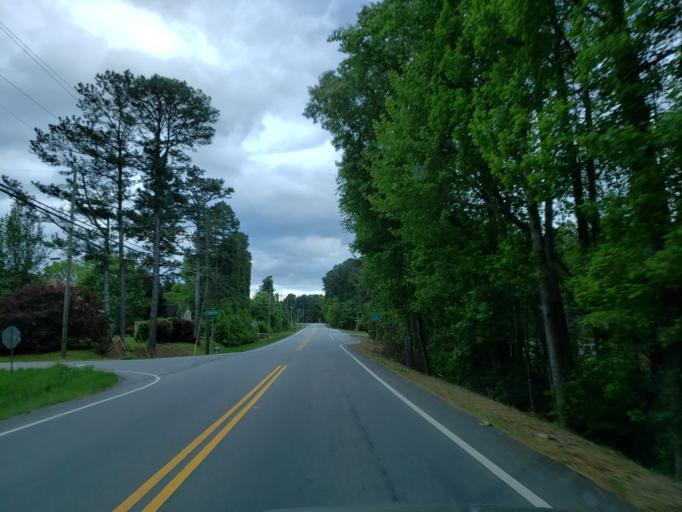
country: US
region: Georgia
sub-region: Paulding County
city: Dallas
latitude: 33.8708
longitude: -84.8512
